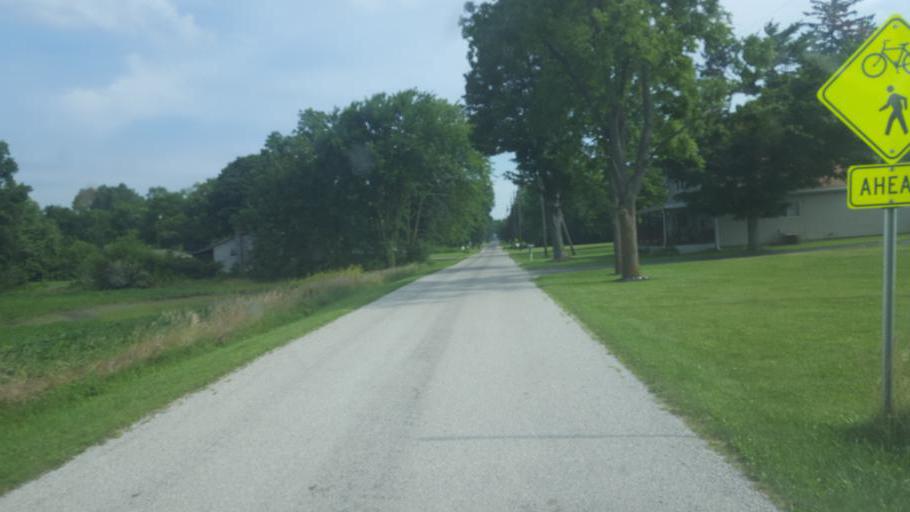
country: US
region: Ohio
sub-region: Marion County
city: Marion
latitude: 40.5965
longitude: -83.2554
